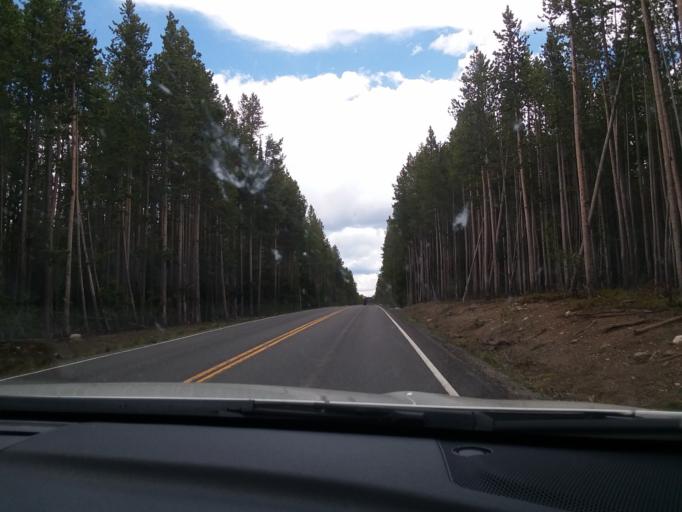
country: US
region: Idaho
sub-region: Teton County
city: Driggs
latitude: 44.1732
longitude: -110.6622
